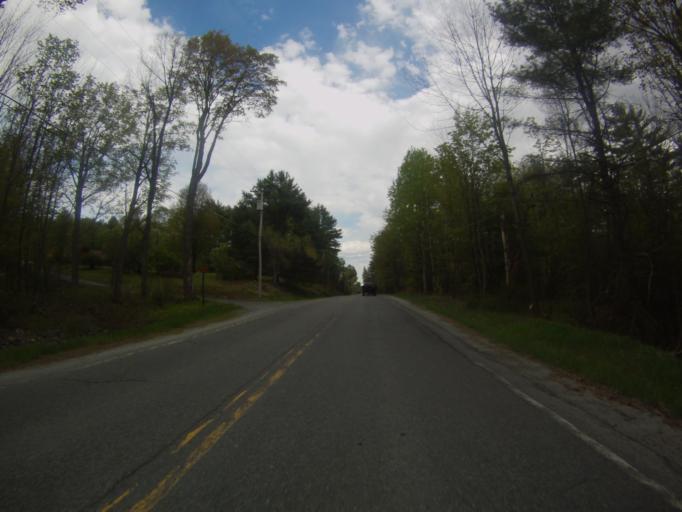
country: US
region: New York
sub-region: Essex County
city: Mineville
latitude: 44.0717
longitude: -73.5227
